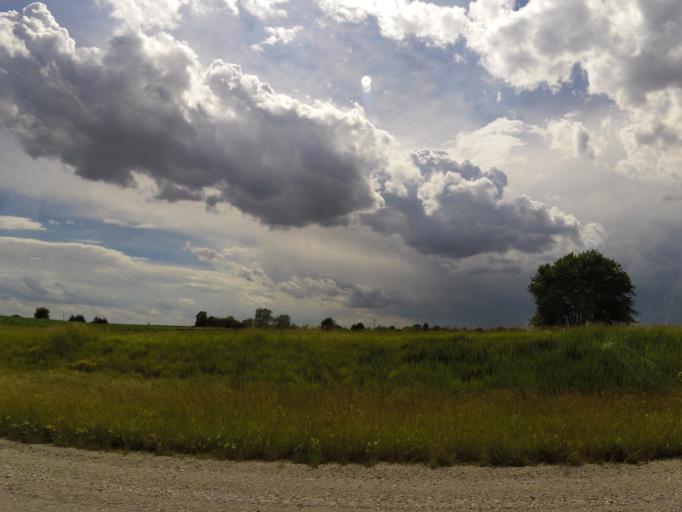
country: US
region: Iowa
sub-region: Washington County
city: Washington
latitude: 41.3001
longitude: -91.5364
